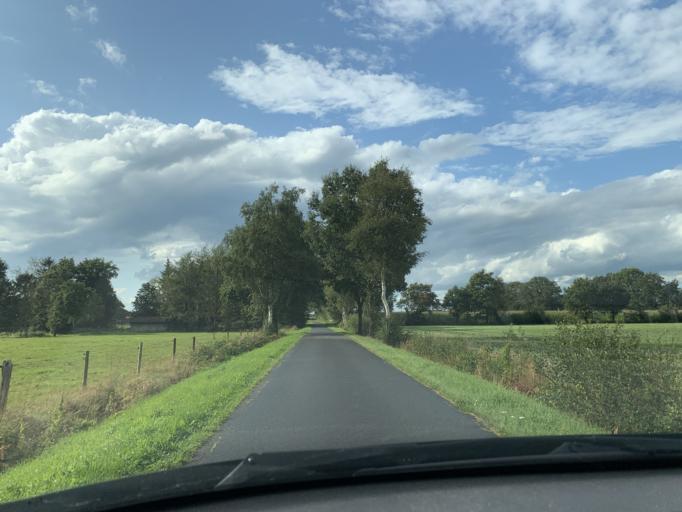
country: DE
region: Lower Saxony
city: Westerstede
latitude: 53.3045
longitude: 8.0041
